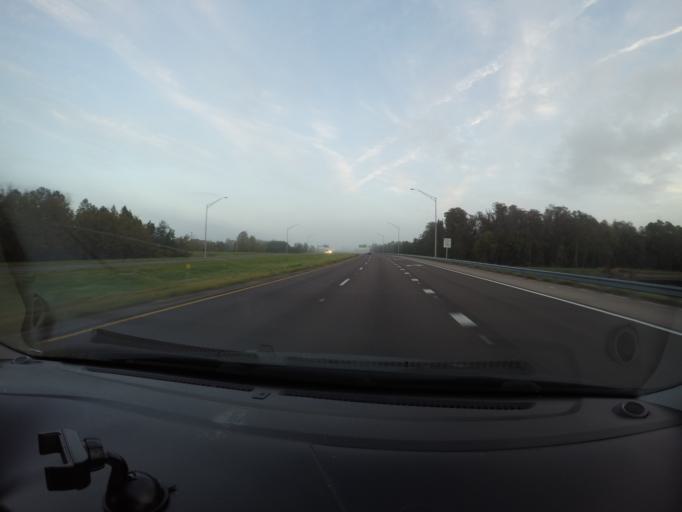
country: US
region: Florida
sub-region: Orange County
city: Conway
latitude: 28.4178
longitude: -81.2271
